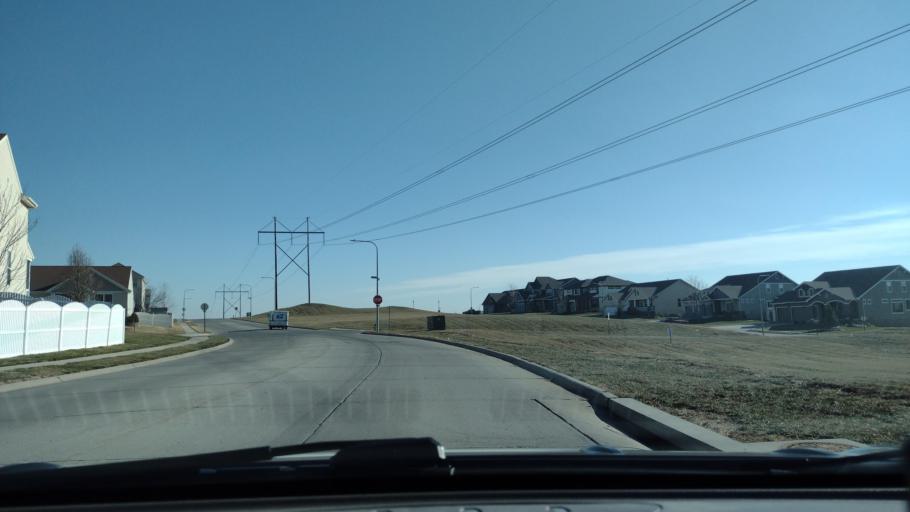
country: US
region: Nebraska
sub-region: Sarpy County
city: La Vista
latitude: 41.1695
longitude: -96.0167
